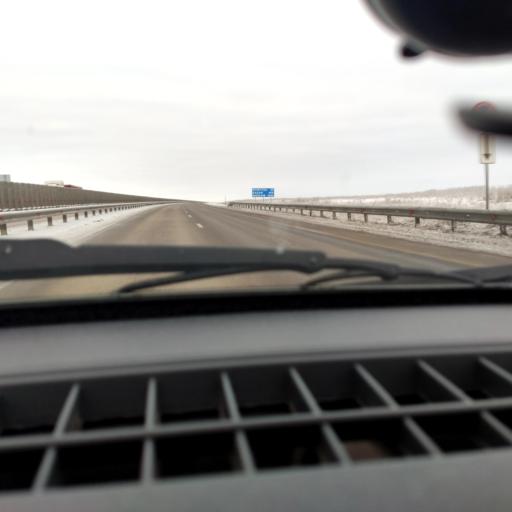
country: RU
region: Bashkortostan
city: Kushnarenkovo
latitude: 55.0831
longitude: 55.2638
